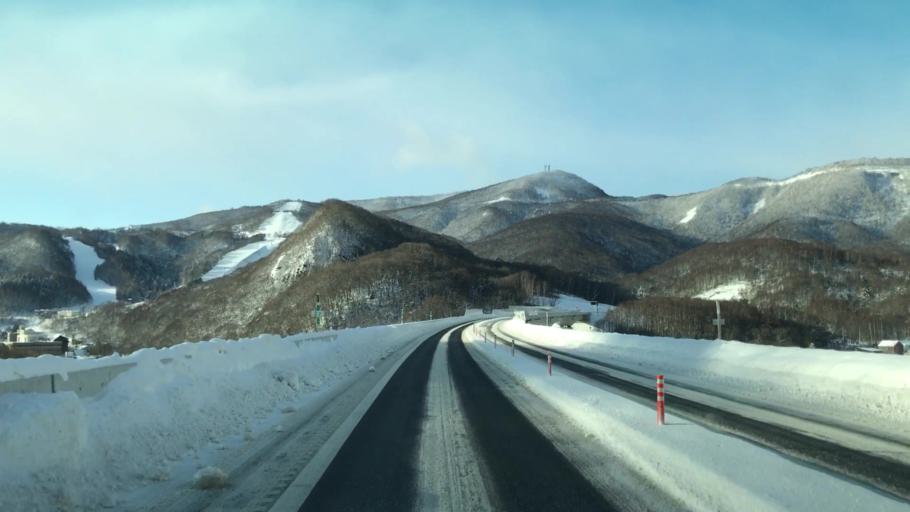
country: JP
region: Hokkaido
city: Otaru
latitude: 43.1544
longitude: 141.0453
